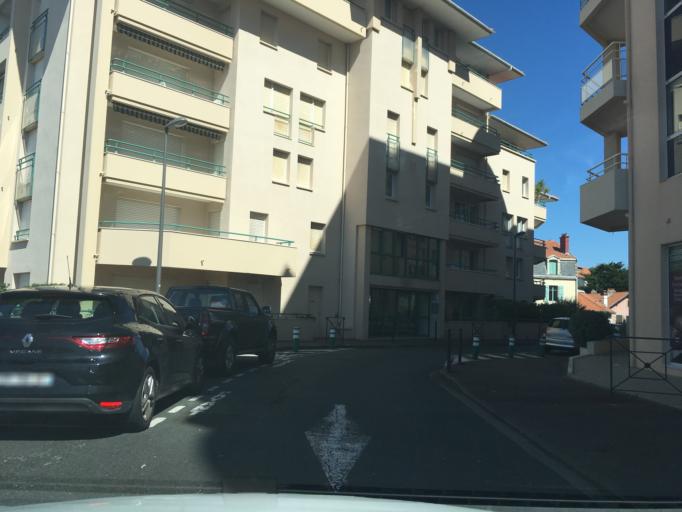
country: FR
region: Aquitaine
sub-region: Departement des Pyrenees-Atlantiques
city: Biarritz
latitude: 43.4793
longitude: -1.5571
